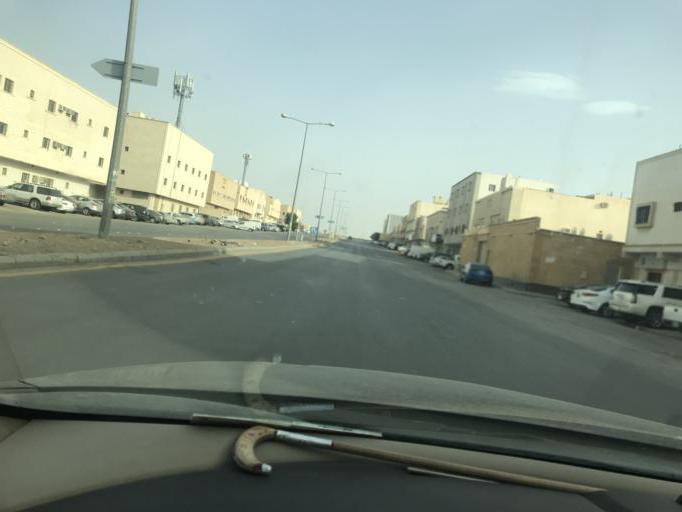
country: SA
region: Ar Riyad
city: Riyadh
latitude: 24.7840
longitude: 46.7144
